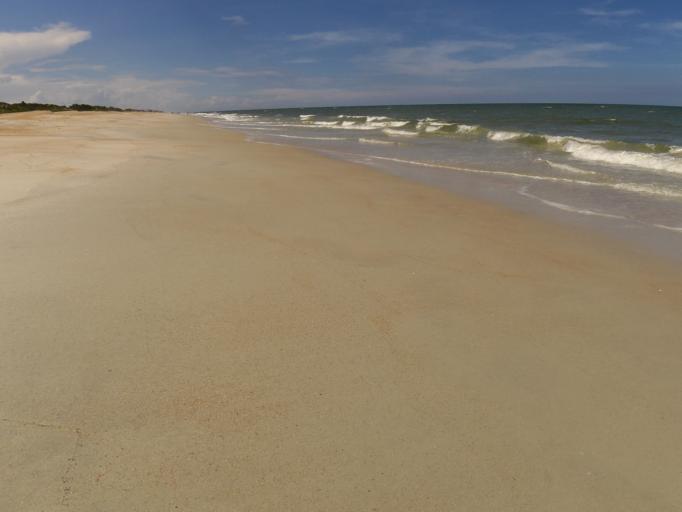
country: US
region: Florida
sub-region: Saint Johns County
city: Palm Valley
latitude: 30.1113
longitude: -81.3431
